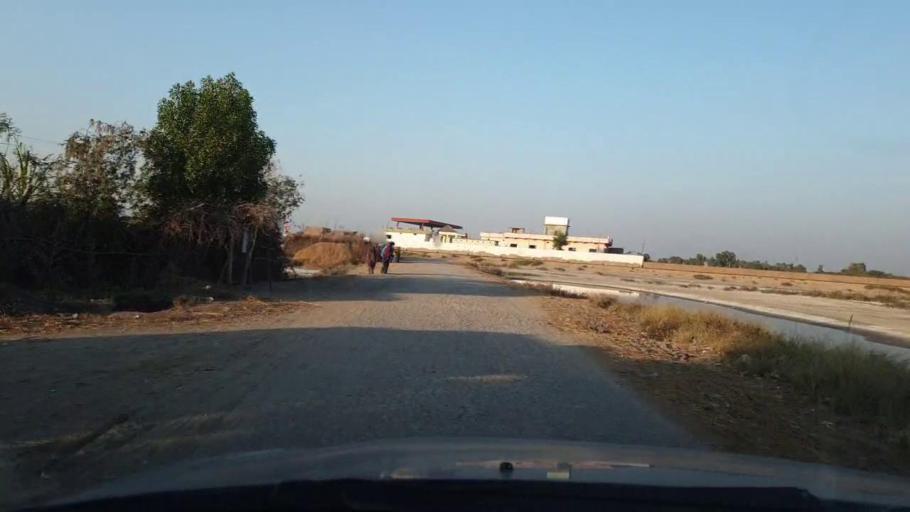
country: PK
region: Sindh
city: Matli
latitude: 25.0429
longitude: 68.6340
